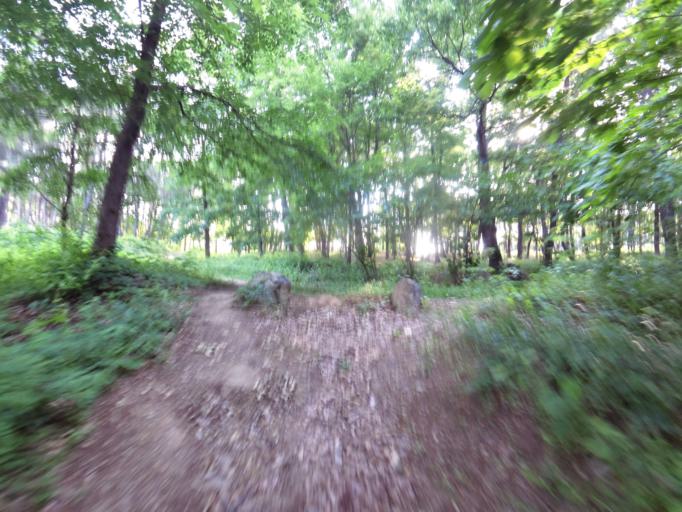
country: KR
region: Gyeongsangbuk-do
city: Gyeongsan-si
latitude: 35.8366
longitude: 128.7618
